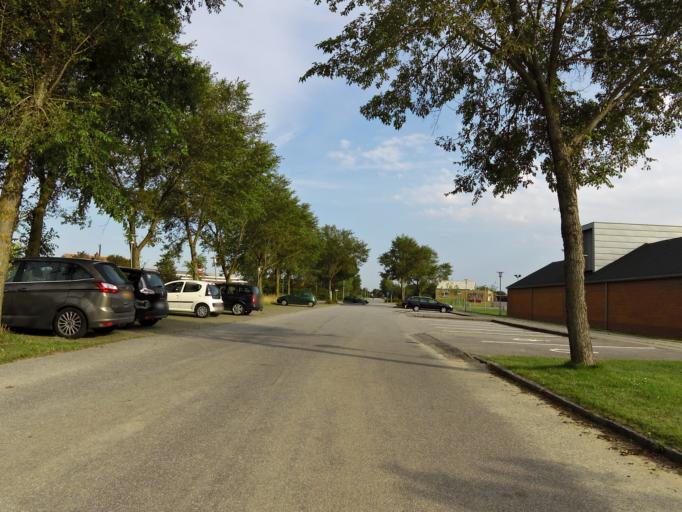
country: DK
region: South Denmark
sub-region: Esbjerg Kommune
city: Ribe
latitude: 55.3238
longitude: 8.7622
